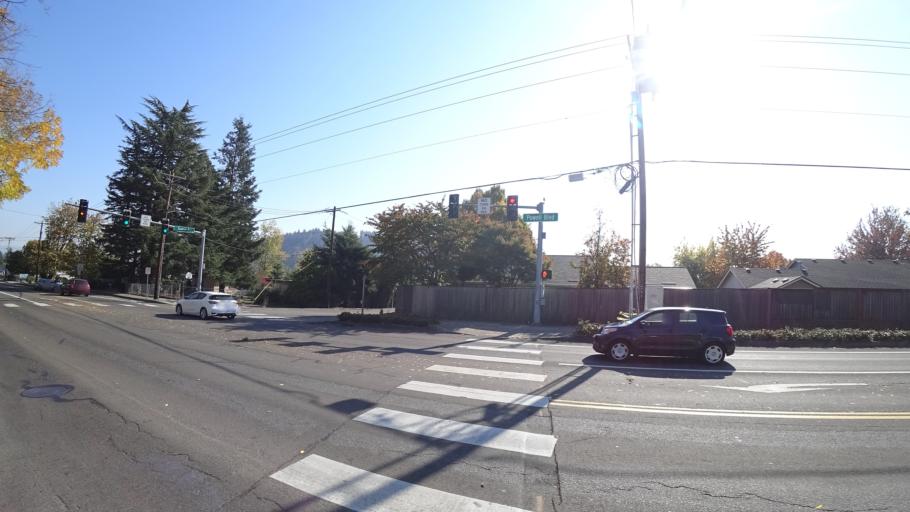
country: US
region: Oregon
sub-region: Multnomah County
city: Gresham
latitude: 45.4971
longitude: -122.4473
